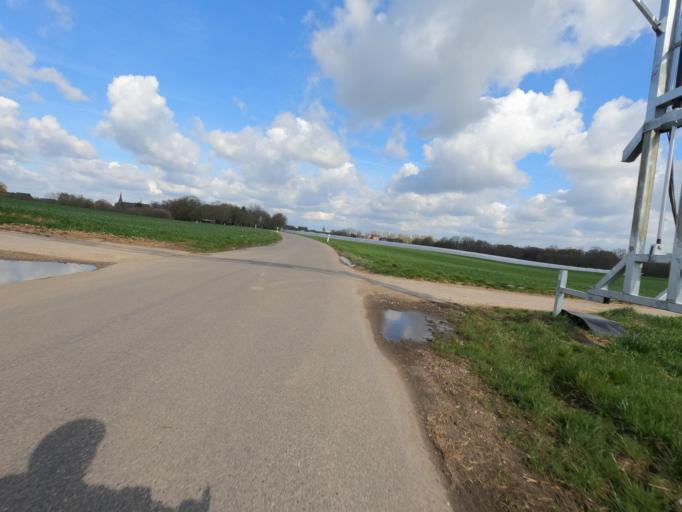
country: DE
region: North Rhine-Westphalia
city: Erkelenz
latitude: 51.0290
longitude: 6.3331
